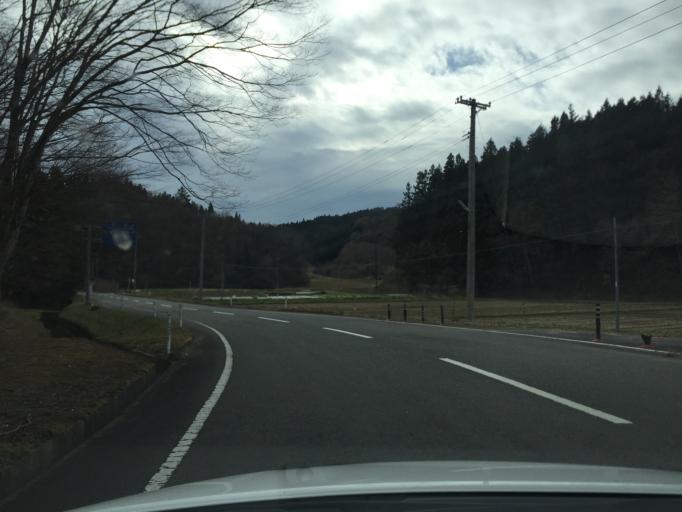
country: JP
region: Fukushima
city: Funehikimachi-funehiki
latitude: 37.2893
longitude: 140.5994
